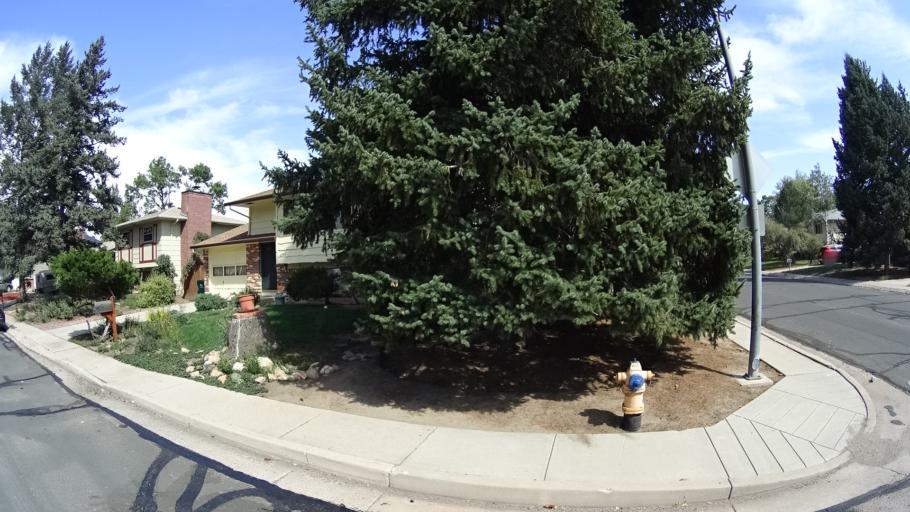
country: US
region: Colorado
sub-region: El Paso County
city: Cimarron Hills
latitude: 38.8962
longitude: -104.7586
